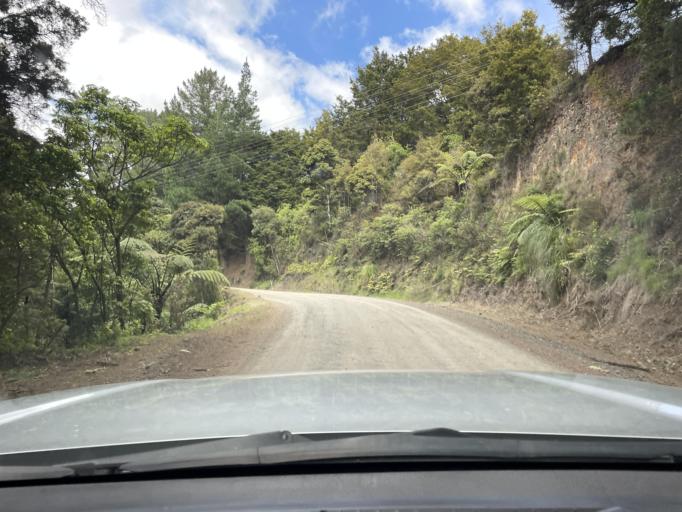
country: NZ
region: Northland
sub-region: Kaipara District
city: Dargaville
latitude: -35.7119
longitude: 173.6261
